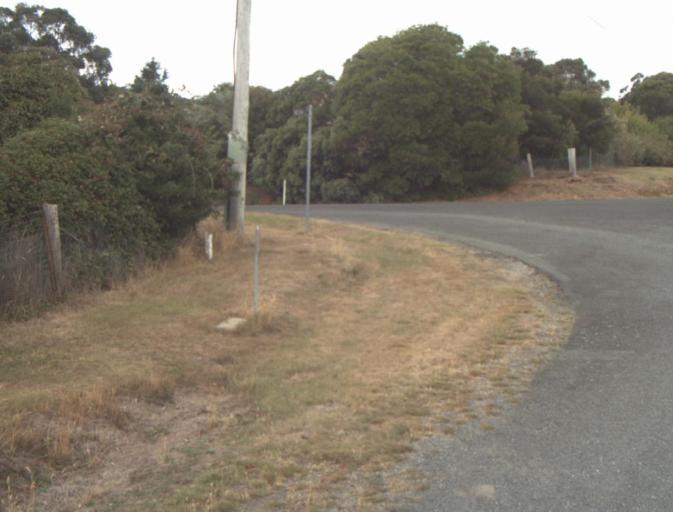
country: AU
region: Tasmania
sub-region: Launceston
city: Mayfield
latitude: -41.2794
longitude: 147.0180
